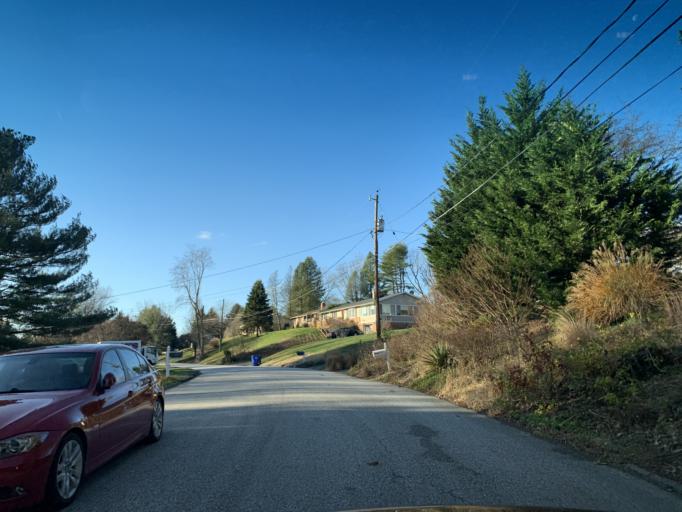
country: US
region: Maryland
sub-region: Harford County
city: South Bel Air
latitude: 39.5606
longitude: -76.2672
